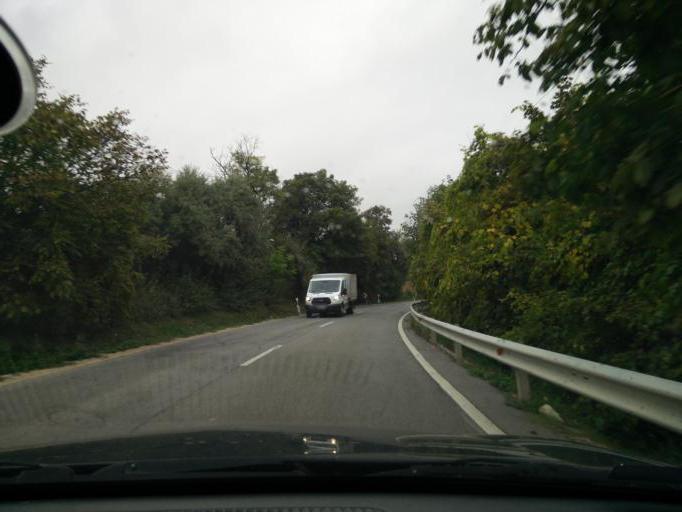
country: HU
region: Komarom-Esztergom
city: Bajna
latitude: 47.6624
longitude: 18.6054
